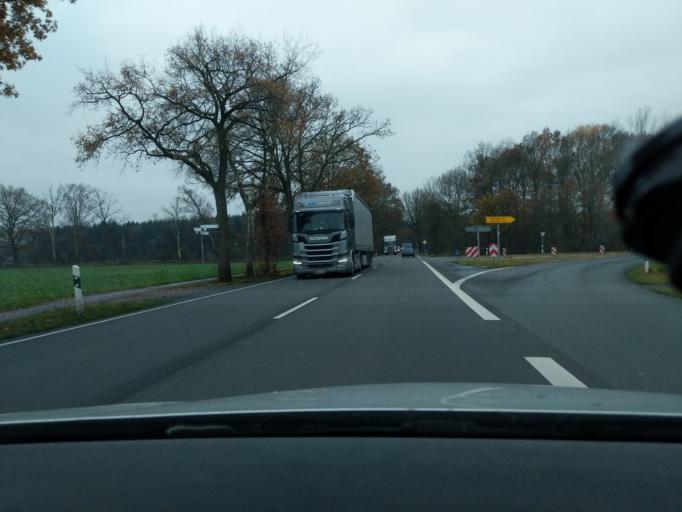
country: DE
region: Lower Saxony
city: Gyhum
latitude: 53.2099
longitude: 9.2913
